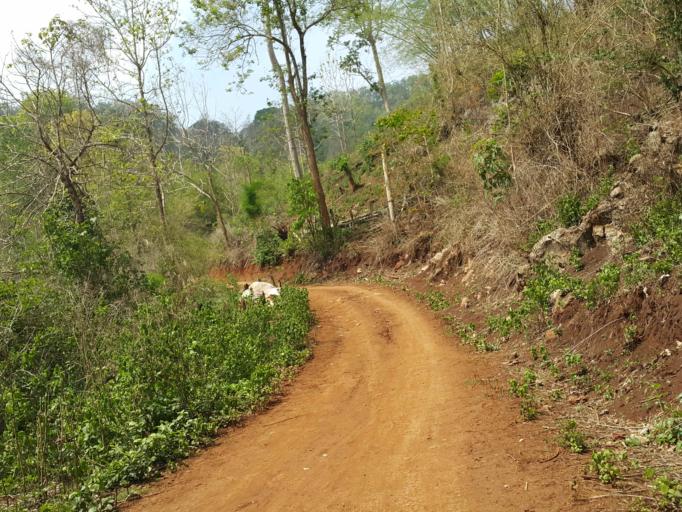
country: TH
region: Chiang Mai
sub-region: Amphoe Chiang Dao
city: Chiang Dao
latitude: 19.3145
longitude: 98.7256
